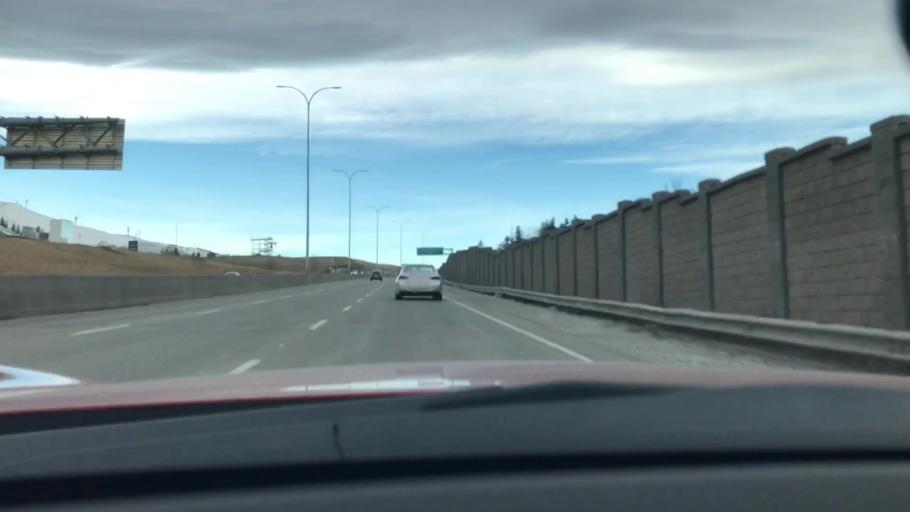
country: CA
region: Alberta
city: Calgary
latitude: 51.0829
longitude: -114.1970
